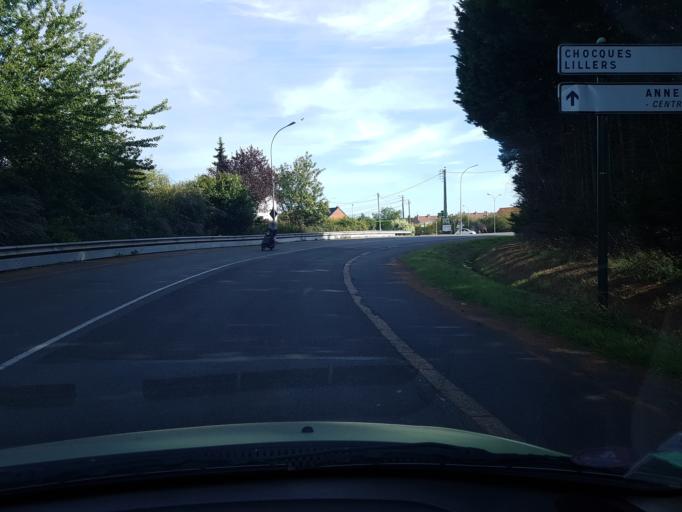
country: FR
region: Nord-Pas-de-Calais
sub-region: Departement du Pas-de-Calais
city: Annezin
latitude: 50.5330
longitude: 2.6102
